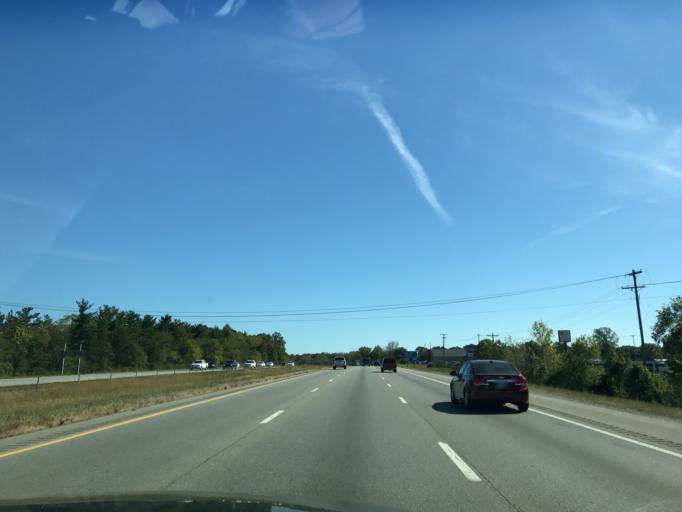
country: US
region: Ohio
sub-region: Franklin County
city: Reynoldsburg
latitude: 39.9313
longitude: -82.8064
